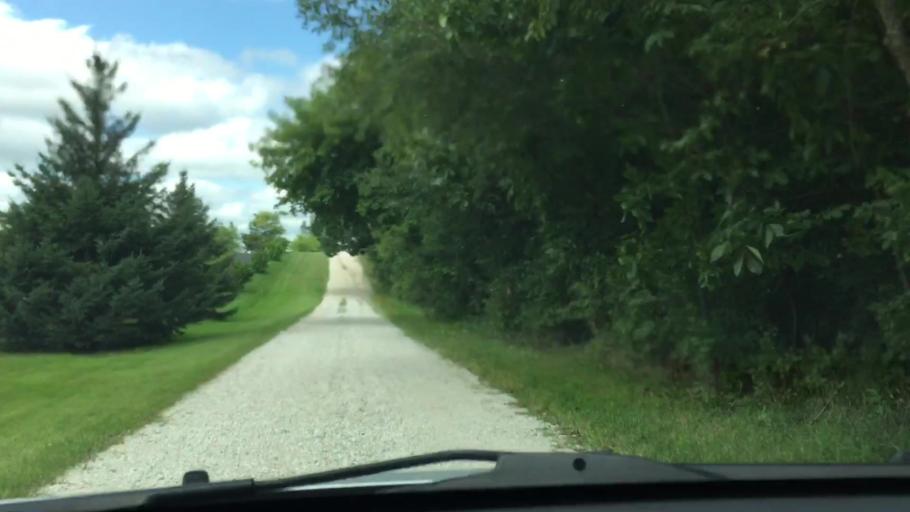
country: US
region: Wisconsin
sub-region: Waukesha County
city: Merton
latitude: 43.1221
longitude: -88.3179
